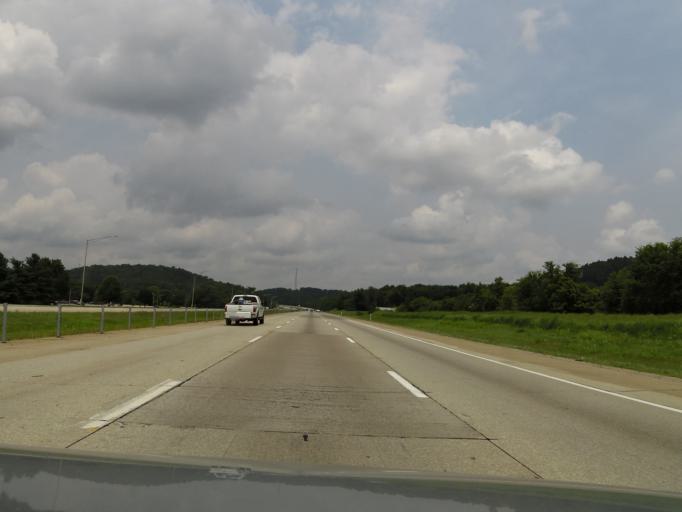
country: US
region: Kentucky
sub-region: Bullitt County
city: Shepherdsville
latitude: 37.9446
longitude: -85.6886
